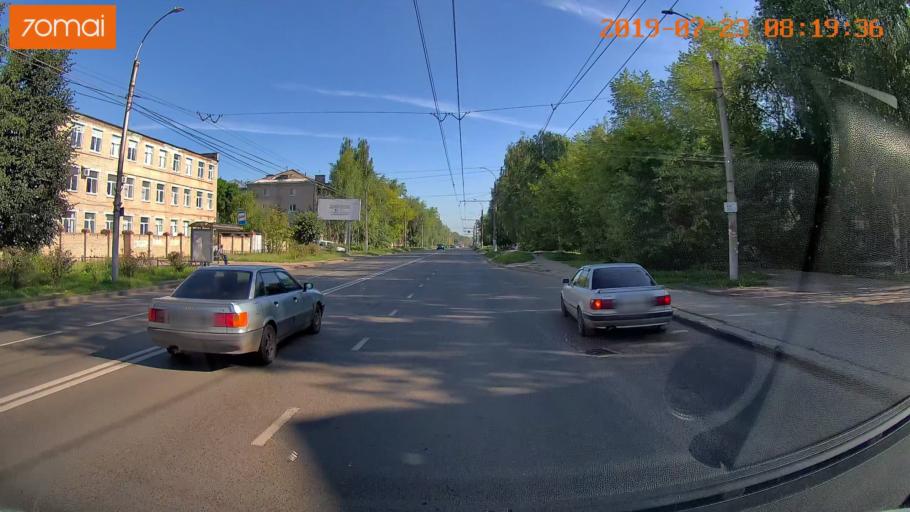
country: RU
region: Ivanovo
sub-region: Gorod Ivanovo
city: Ivanovo
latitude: 56.9678
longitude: 40.9631
